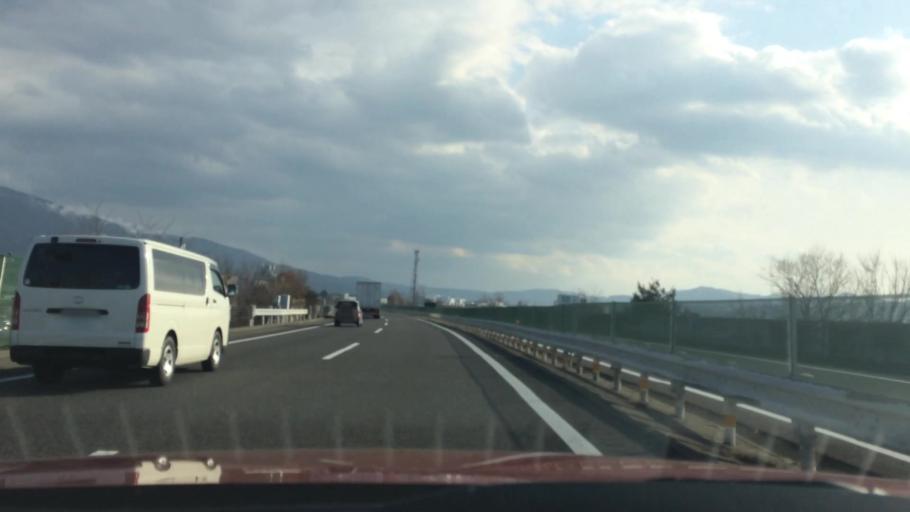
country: JP
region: Nagano
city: Matsumoto
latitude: 36.1745
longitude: 137.9428
